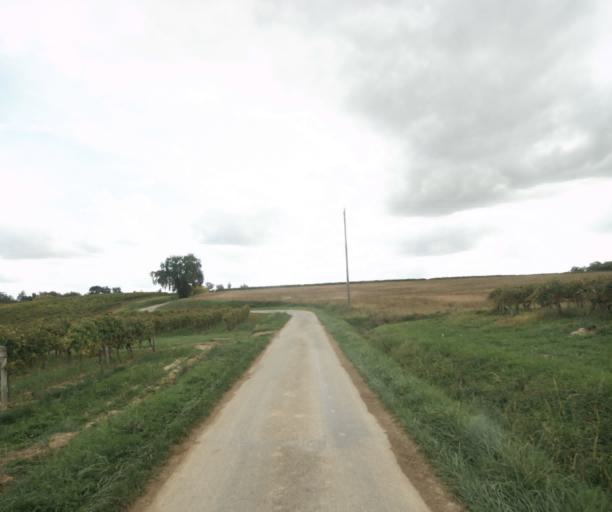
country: FR
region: Midi-Pyrenees
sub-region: Departement du Gers
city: Gondrin
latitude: 43.8696
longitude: 0.2501
